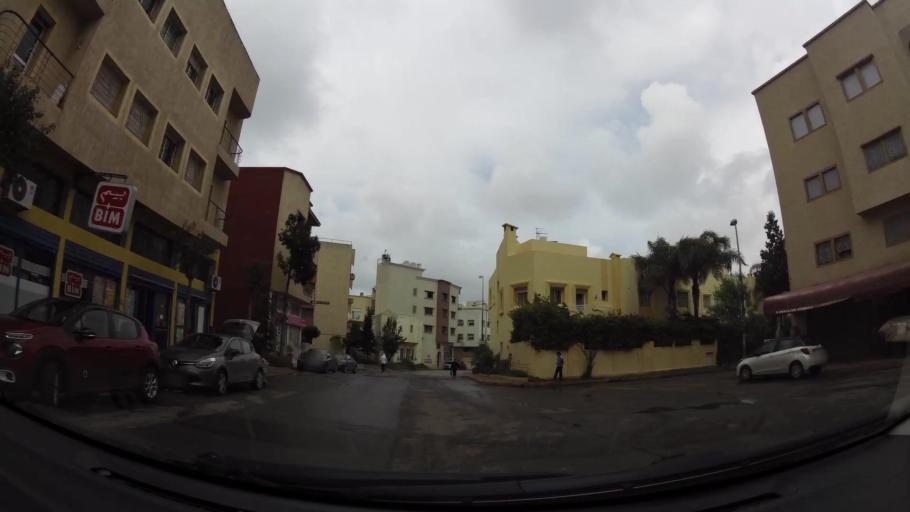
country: MA
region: Grand Casablanca
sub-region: Casablanca
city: Casablanca
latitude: 33.5370
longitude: -7.6508
